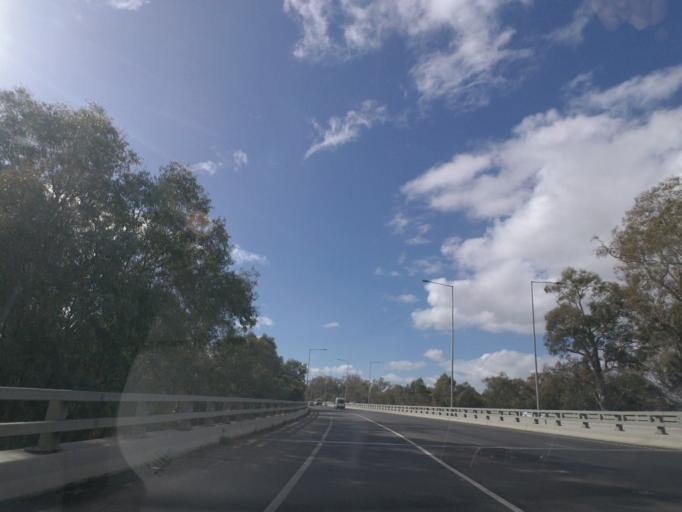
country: AU
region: Victoria
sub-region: Wodonga
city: Wodonga
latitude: -36.1071
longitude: 146.9034
